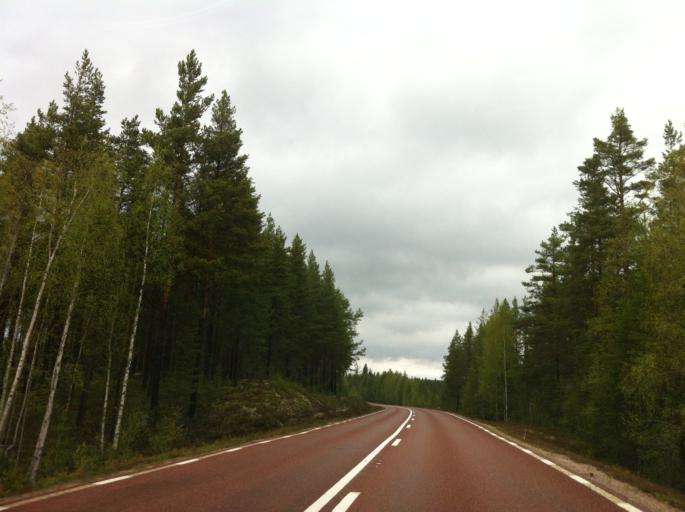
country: SE
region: Jaemtland
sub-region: Harjedalens Kommun
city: Sveg
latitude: 61.9095
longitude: 14.6222
